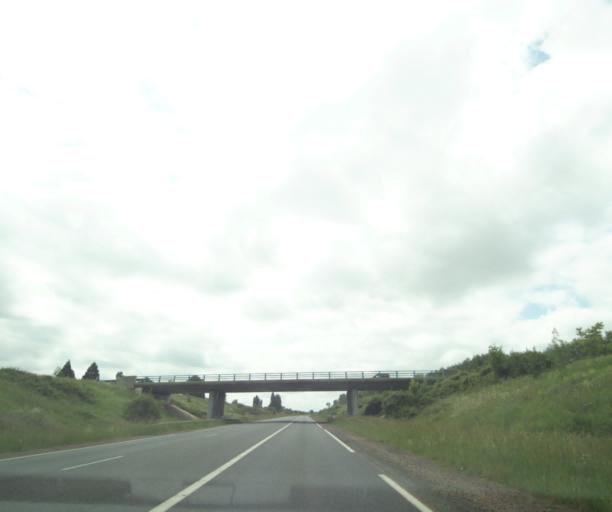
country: FR
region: Poitou-Charentes
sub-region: Departement des Deux-Sevres
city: Saint-Varent
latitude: 46.8280
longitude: -0.2053
